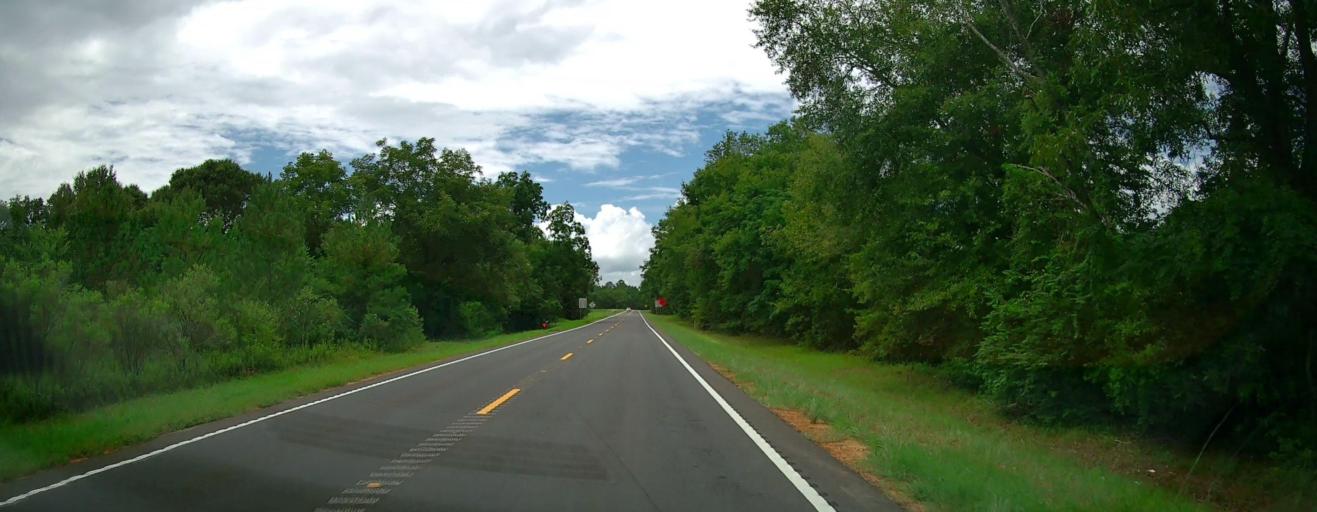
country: US
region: Georgia
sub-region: Wilcox County
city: Rochelle
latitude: 32.0930
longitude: -83.5885
